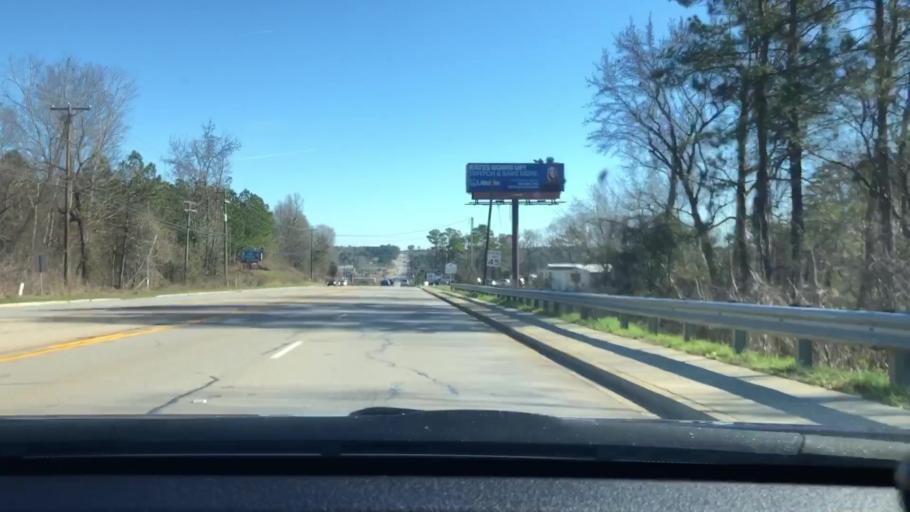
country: US
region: South Carolina
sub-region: Lexington County
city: Oak Grove
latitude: 34.0126
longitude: -81.1791
